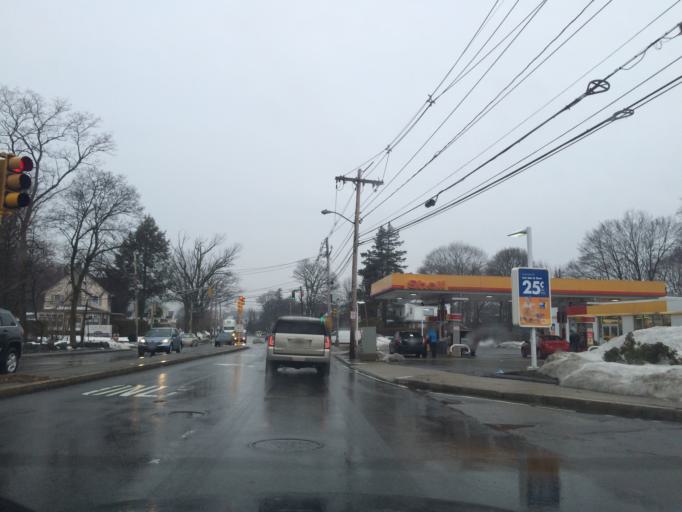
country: US
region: Massachusetts
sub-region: Middlesex County
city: Waltham
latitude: 42.3747
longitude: -71.2105
